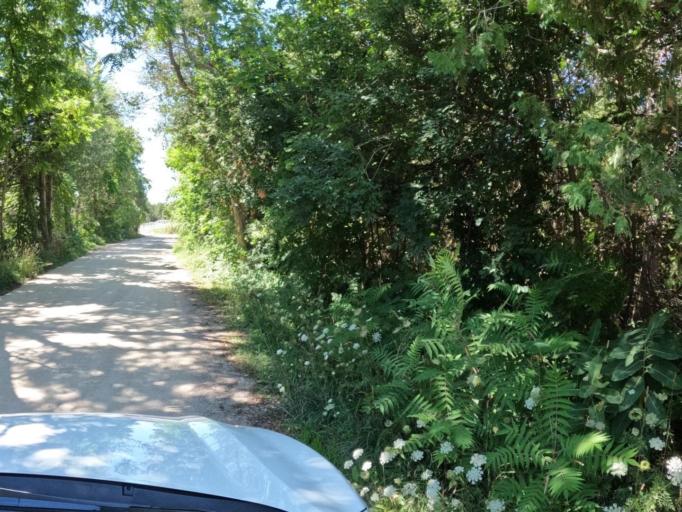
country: CA
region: Ontario
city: Cambridge
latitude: 43.4115
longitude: -80.2634
